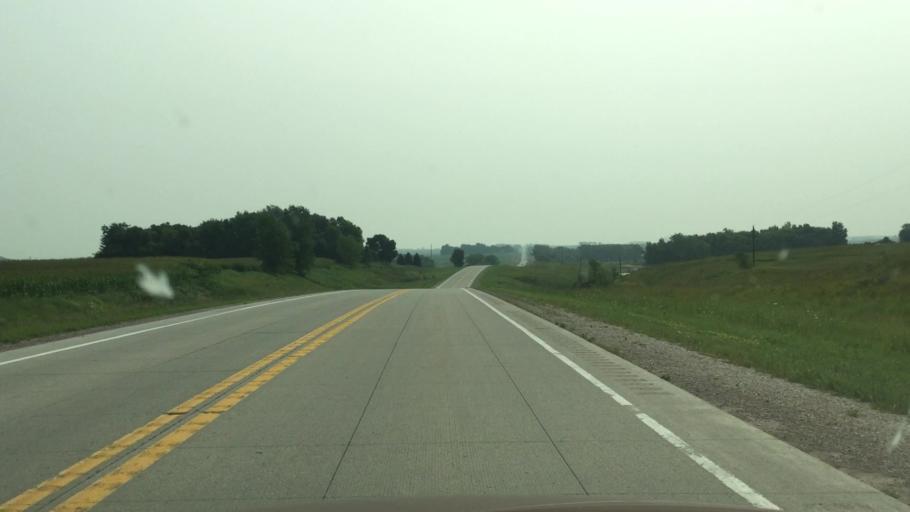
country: US
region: Iowa
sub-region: Osceola County
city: Sibley
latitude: 43.4329
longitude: -95.6230
